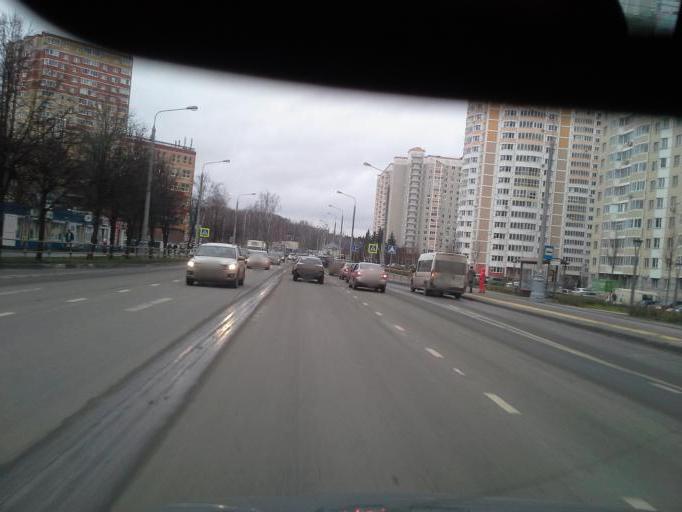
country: RU
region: Moskovskaya
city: Moskovskiy
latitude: 55.6016
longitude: 37.3563
